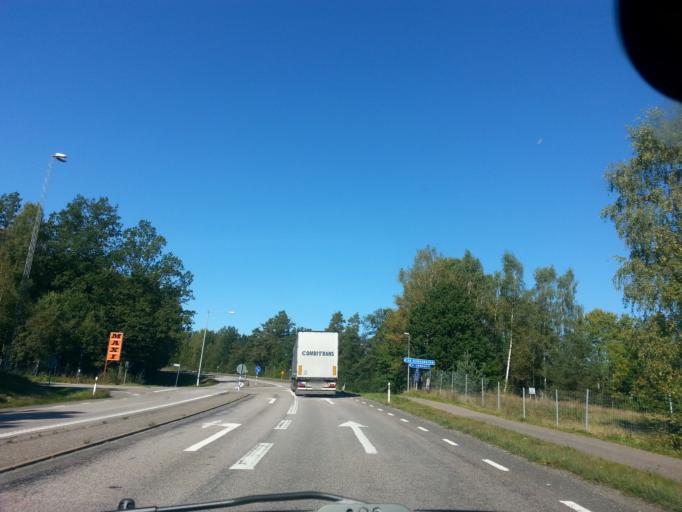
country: SE
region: Vaestra Goetaland
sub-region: Harryda Kommun
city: Ravlanda
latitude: 57.6194
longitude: 12.4344
